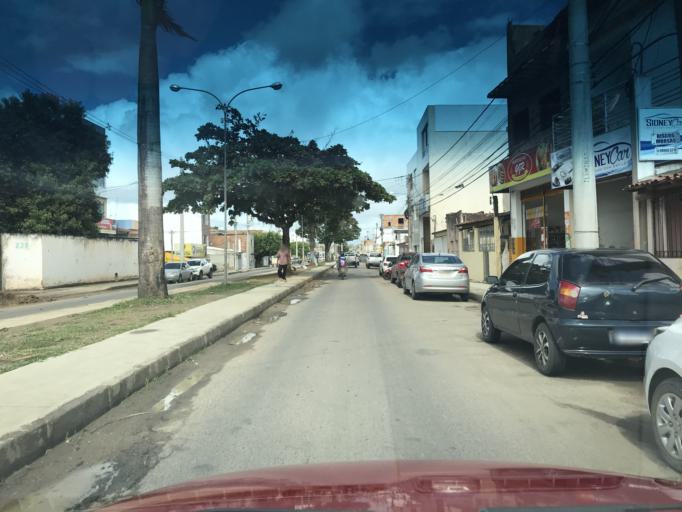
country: BR
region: Bahia
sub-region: Santo Antonio De Jesus
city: Santo Antonio de Jesus
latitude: -12.9688
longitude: -39.2711
